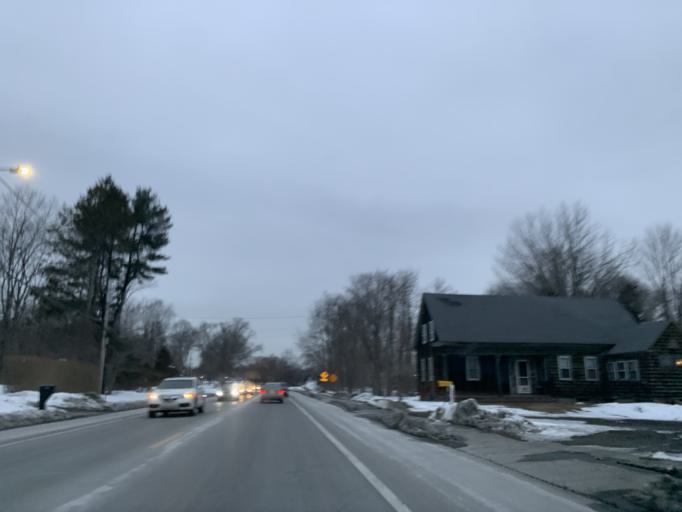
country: US
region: Massachusetts
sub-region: Norfolk County
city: Stoughton
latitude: 42.1080
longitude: -71.0703
